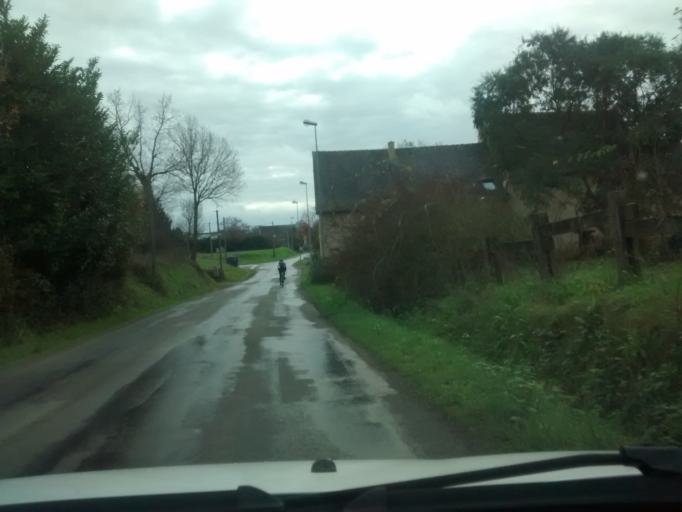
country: FR
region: Brittany
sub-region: Departement d'Ille-et-Vilaine
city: Cesson-Sevigne
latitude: 48.1368
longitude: -1.6002
